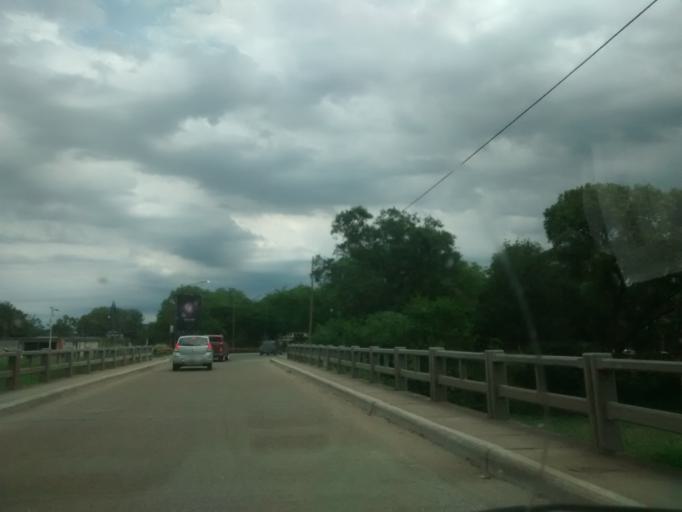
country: AR
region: Chaco
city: Resistencia
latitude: -27.4353
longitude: -58.9823
